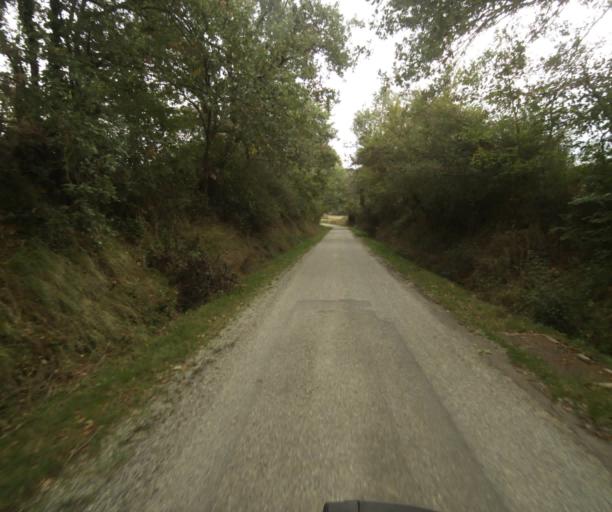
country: FR
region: Midi-Pyrenees
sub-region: Departement du Tarn-et-Garonne
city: Verdun-sur-Garonne
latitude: 43.8493
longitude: 1.1140
